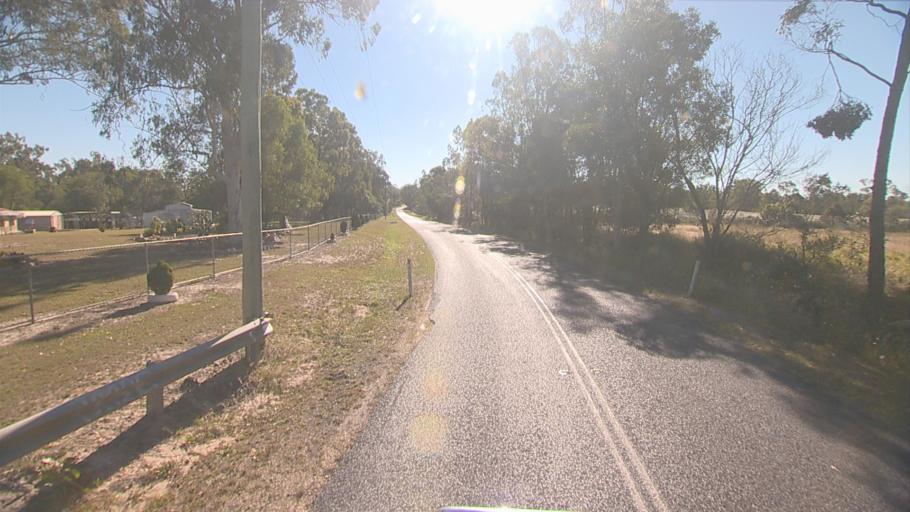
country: AU
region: Queensland
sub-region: Logan
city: Chambers Flat
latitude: -27.7436
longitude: 153.0827
